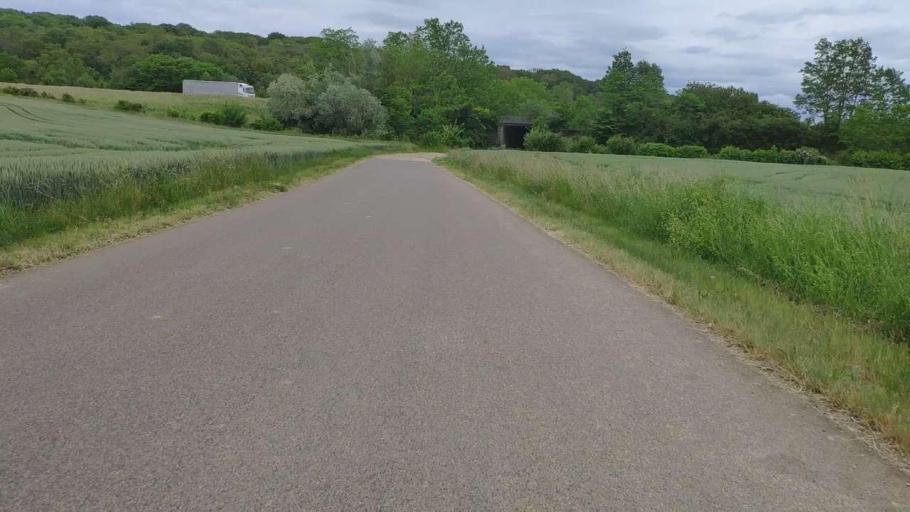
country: FR
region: Franche-Comte
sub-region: Departement du Jura
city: Bletterans
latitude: 46.7699
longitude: 5.5123
